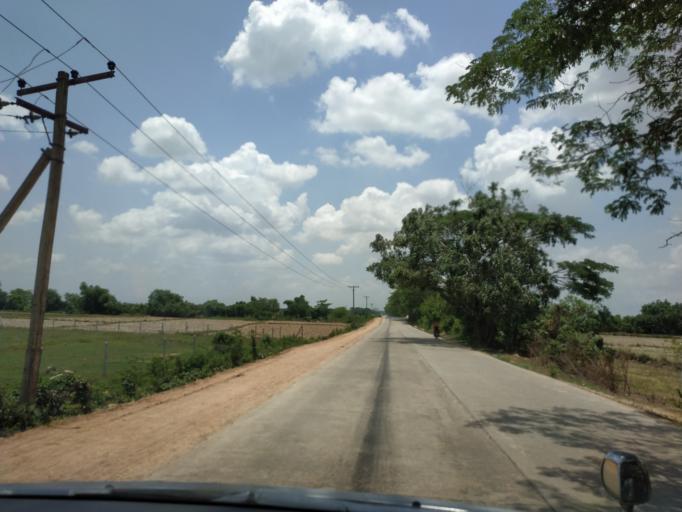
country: MM
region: Bago
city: Bago
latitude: 17.4794
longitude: 96.4905
